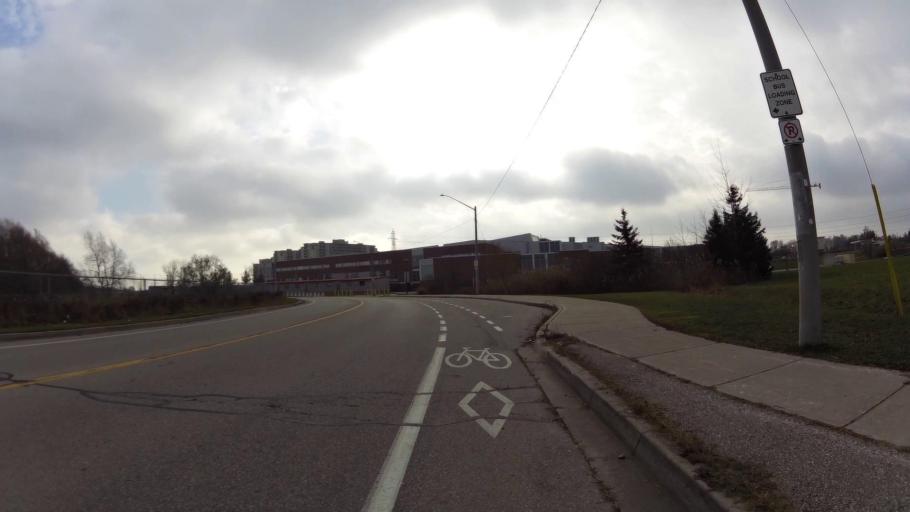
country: CA
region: Ontario
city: Kitchener
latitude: 43.4216
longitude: -80.4679
